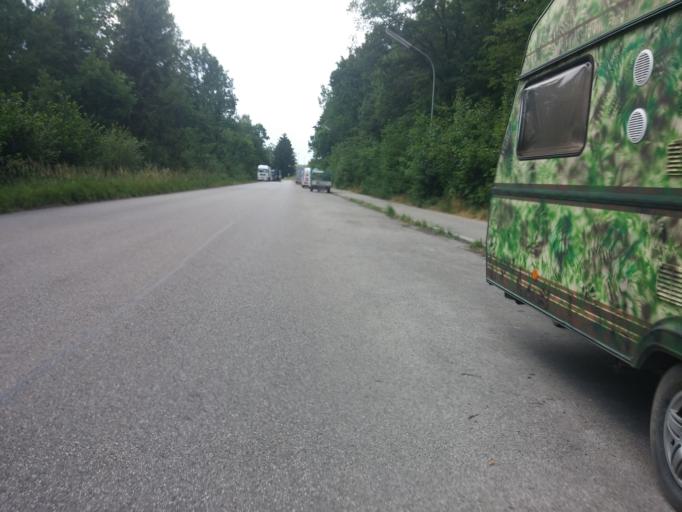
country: DE
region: Bavaria
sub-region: Upper Bavaria
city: Unterhaching
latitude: 48.0848
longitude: 11.6009
